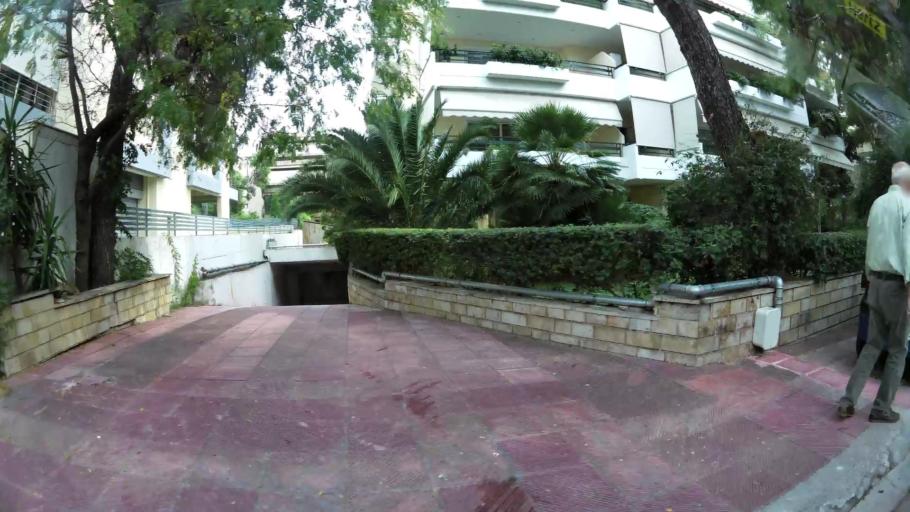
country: GR
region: Attica
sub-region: Nomarchia Athinas
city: Chaidari
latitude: 38.0152
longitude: 23.6477
